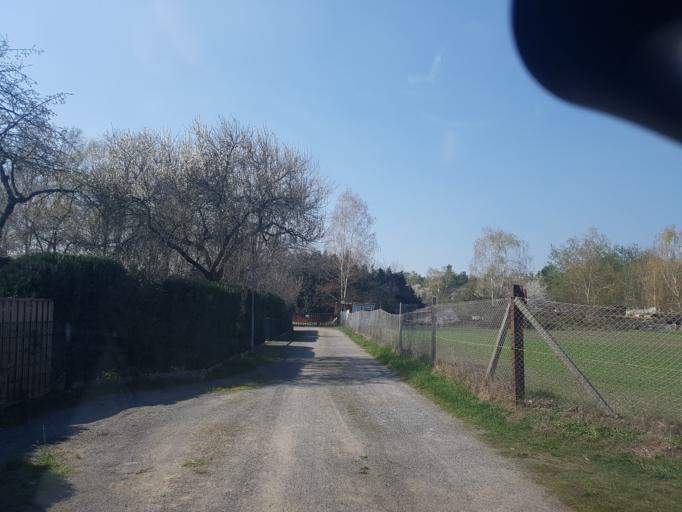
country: DE
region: Brandenburg
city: Finsterwalde
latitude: 51.6421
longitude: 13.6805
